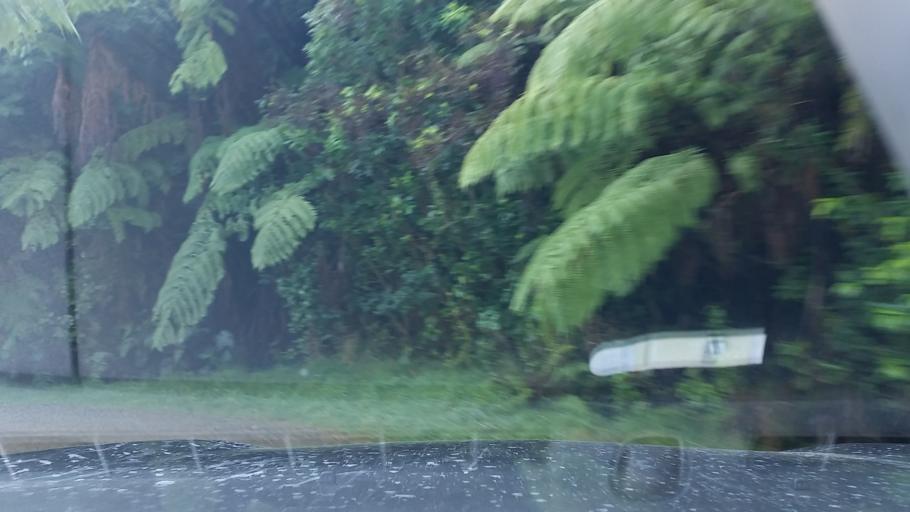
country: NZ
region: Marlborough
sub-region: Marlborough District
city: Picton
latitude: -41.1192
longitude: 173.9951
